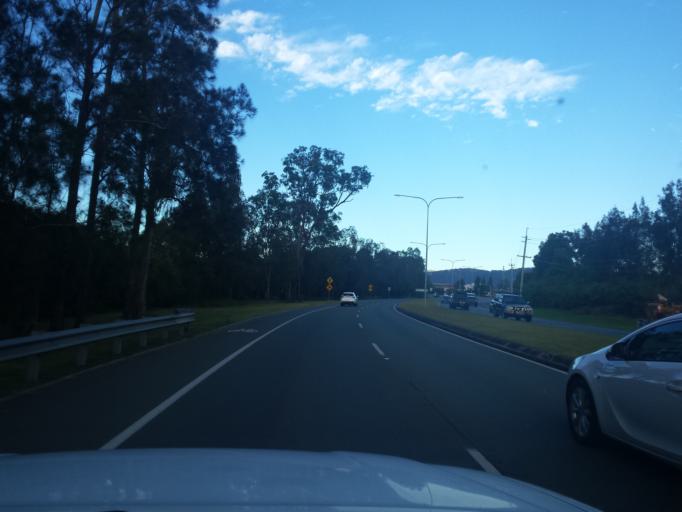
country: AU
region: Queensland
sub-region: Gold Coast
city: Oxenford
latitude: -27.8823
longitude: 153.3271
